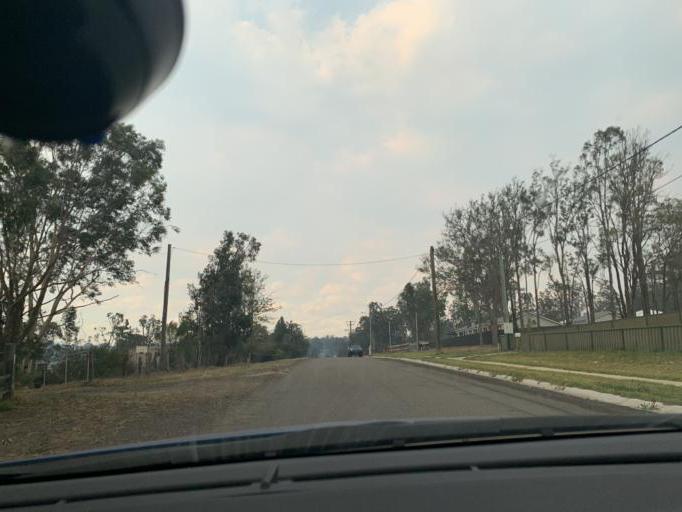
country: AU
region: New South Wales
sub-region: Cessnock
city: Cessnock
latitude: -32.9232
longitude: 151.3100
